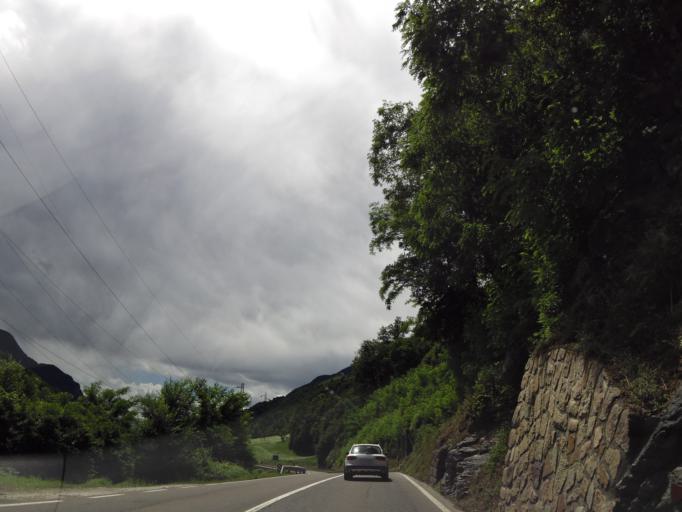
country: IT
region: Trentino-Alto Adige
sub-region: Bolzano
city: Villandro
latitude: 46.6189
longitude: 11.5394
